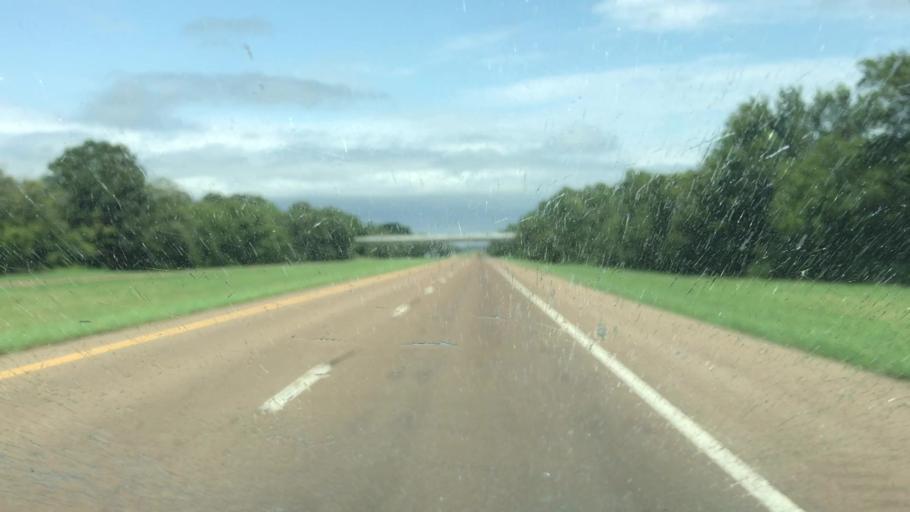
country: US
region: Tennessee
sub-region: Obion County
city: South Fulton
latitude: 36.4809
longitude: -88.9438
